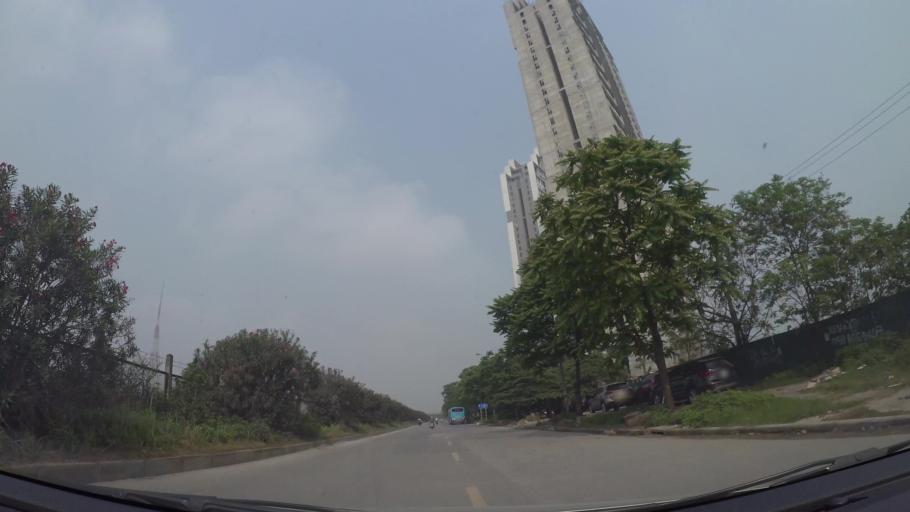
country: VN
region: Ha Noi
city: Thanh Xuan
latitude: 21.0056
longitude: 105.7709
